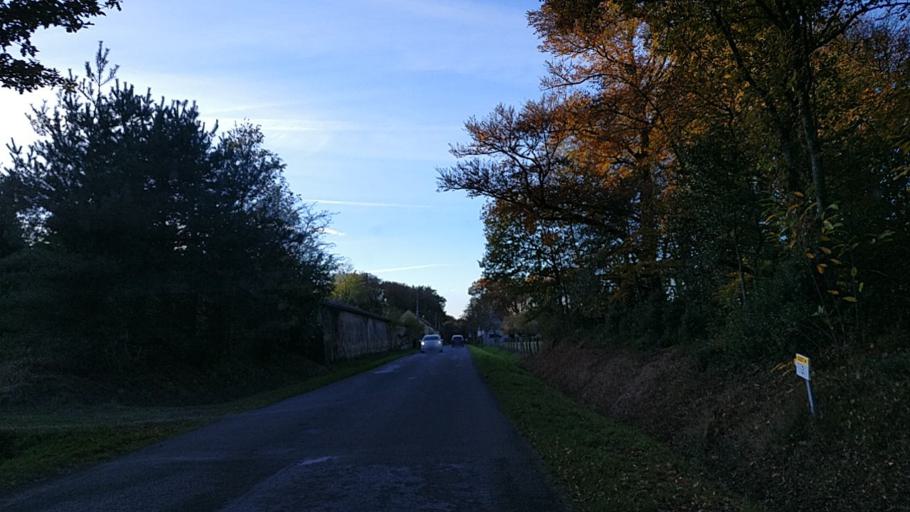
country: FR
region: Brittany
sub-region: Departement d'Ille-et-Vilaine
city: Saint-Sulpice-la-Foret
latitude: 48.1943
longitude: -1.5745
